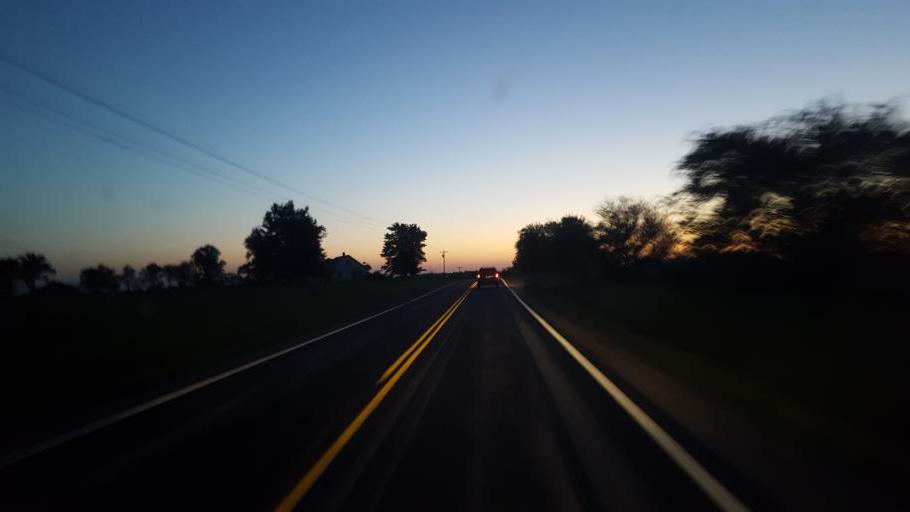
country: US
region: Missouri
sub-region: Mercer County
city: Princeton
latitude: 40.4318
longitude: -93.4799
